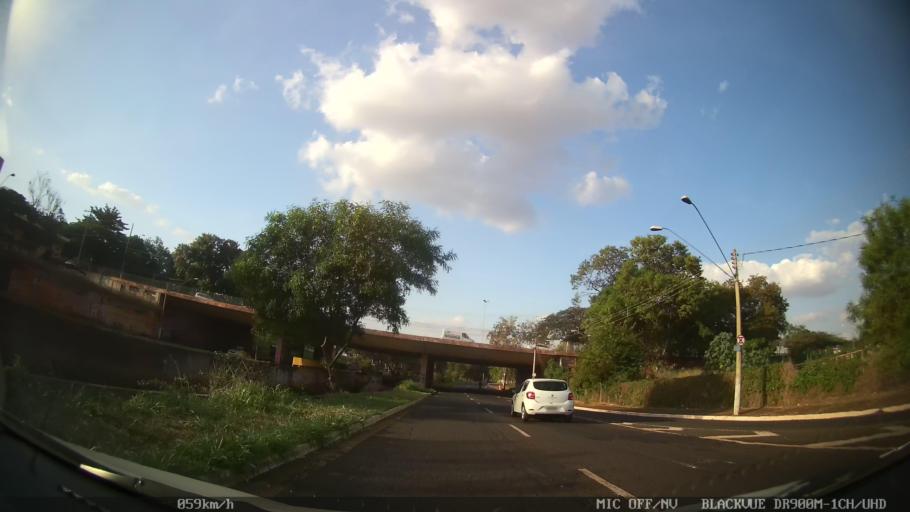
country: BR
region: Sao Paulo
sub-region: Ribeirao Preto
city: Ribeirao Preto
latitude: -21.1609
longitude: -47.8146
